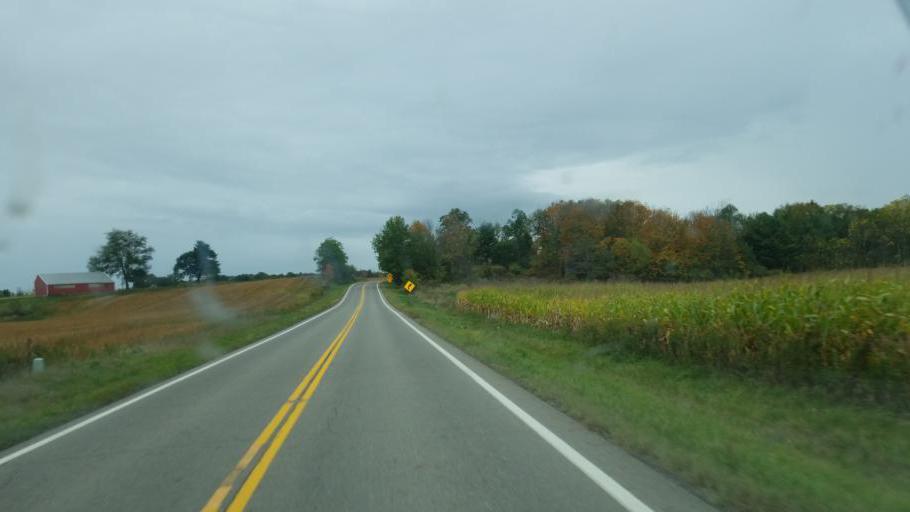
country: US
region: Ohio
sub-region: Ashland County
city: Ashland
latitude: 40.9560
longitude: -82.3705
